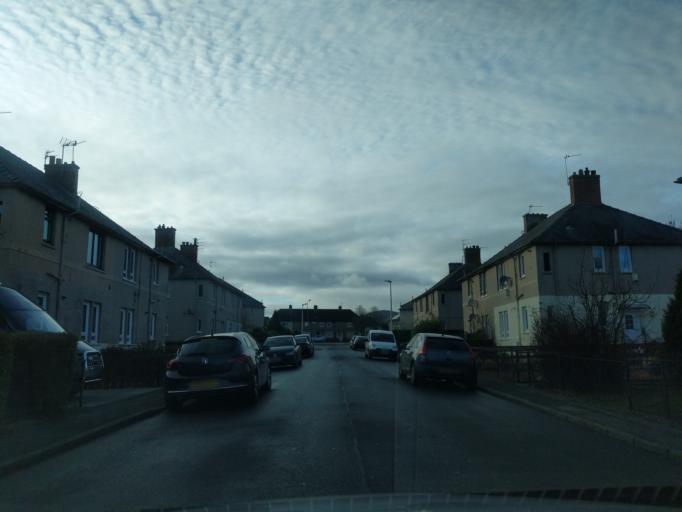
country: GB
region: Scotland
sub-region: Midlothian
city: Loanhead
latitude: 55.8766
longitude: -3.1614
